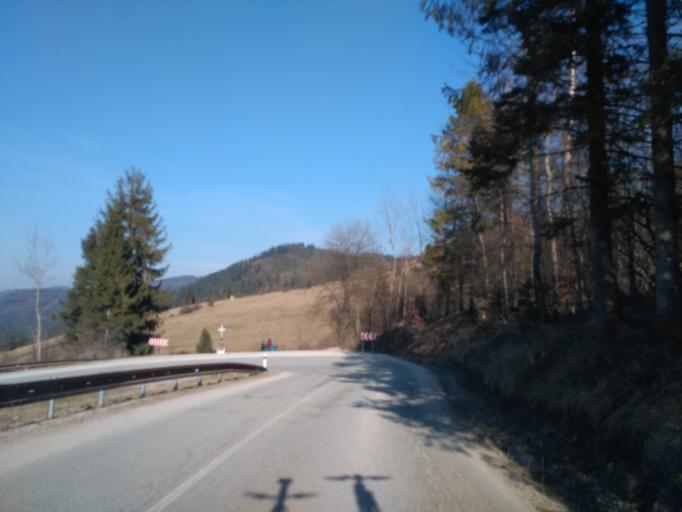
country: SK
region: Kosicky
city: Medzev
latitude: 48.7260
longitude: 20.7424
